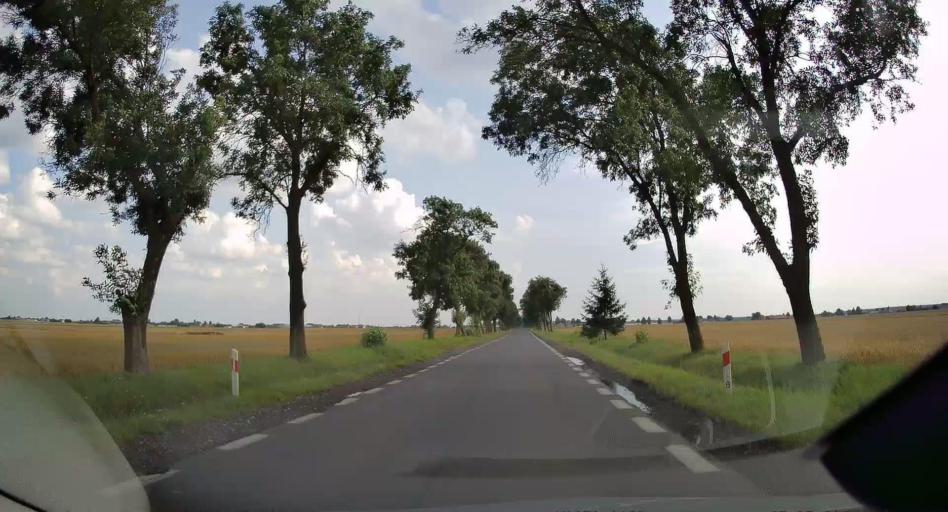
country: PL
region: Lodz Voivodeship
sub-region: Powiat tomaszowski
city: Rzeczyca
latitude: 51.6203
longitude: 20.2929
